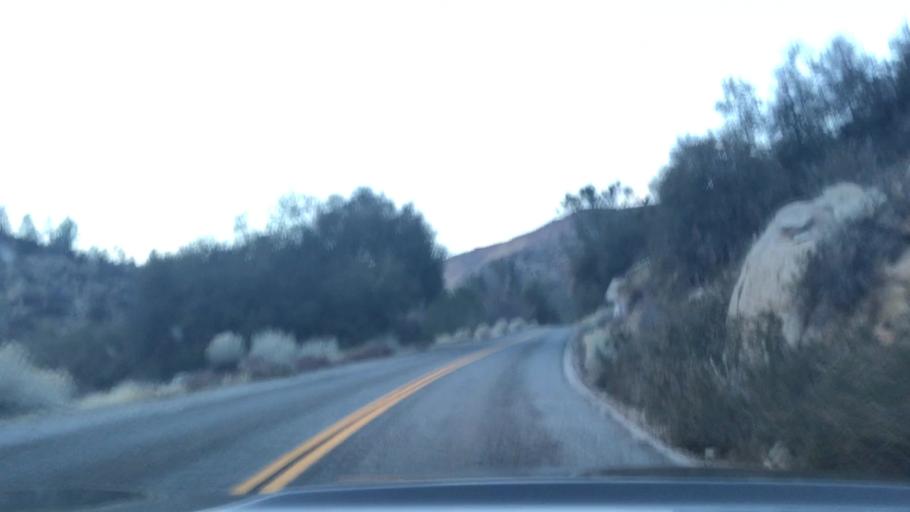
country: US
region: California
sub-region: Kern County
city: Kernville
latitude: 35.8944
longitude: -118.4657
